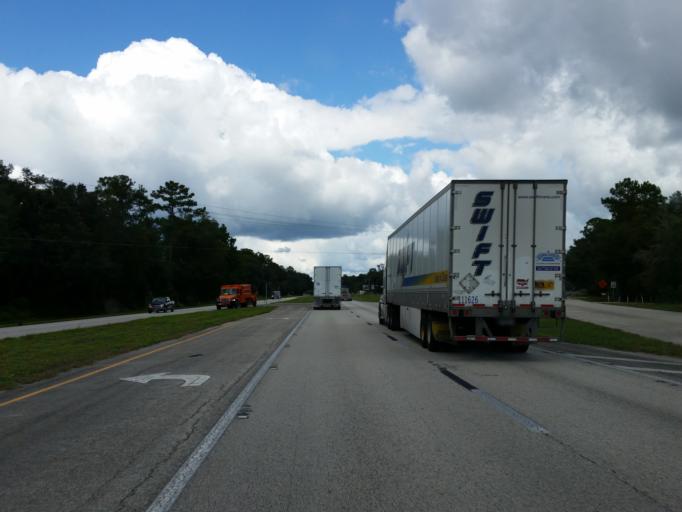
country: US
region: Florida
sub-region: Alachua County
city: Waldo
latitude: 29.8498
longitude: -82.1578
